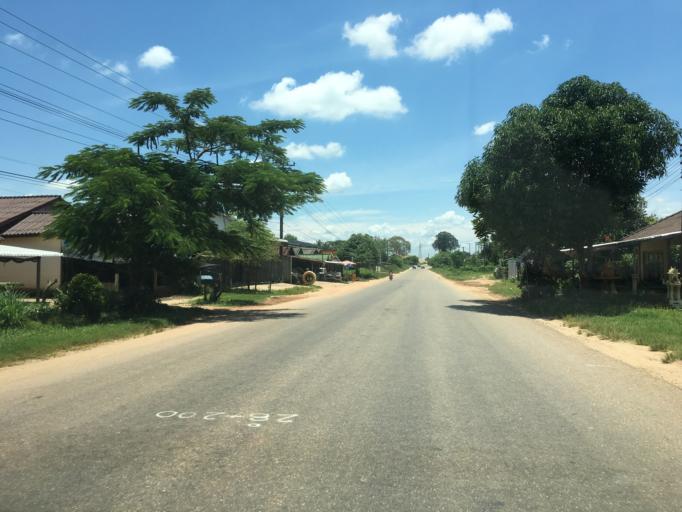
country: LA
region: Vientiane
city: Muang Phon-Hong
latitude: 18.2613
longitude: 102.4858
